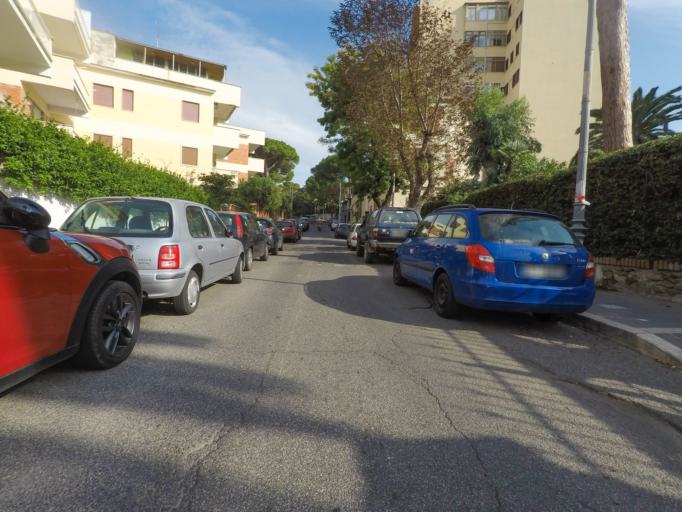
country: IT
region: Latium
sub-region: Citta metropolitana di Roma Capitale
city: Santa Marinella
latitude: 42.0346
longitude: 11.8628
